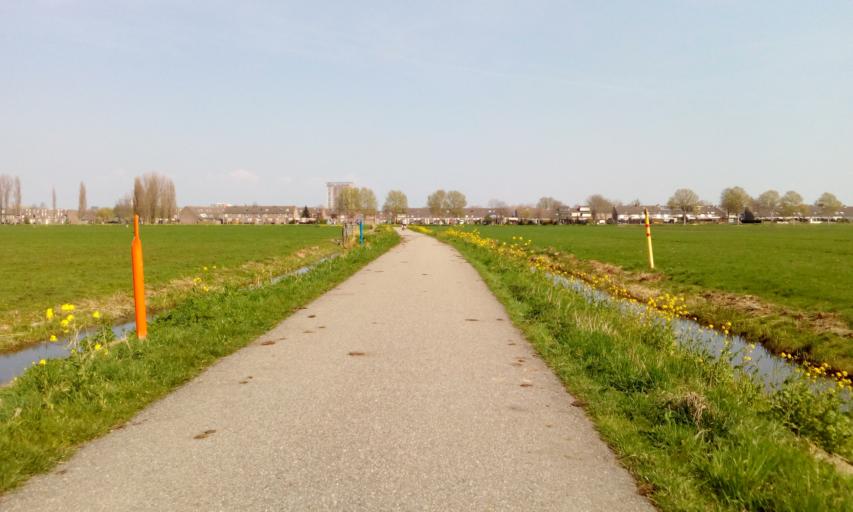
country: NL
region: South Holland
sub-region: Gemeente Spijkenisse
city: Spijkenisse
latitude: 51.8285
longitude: 4.3053
